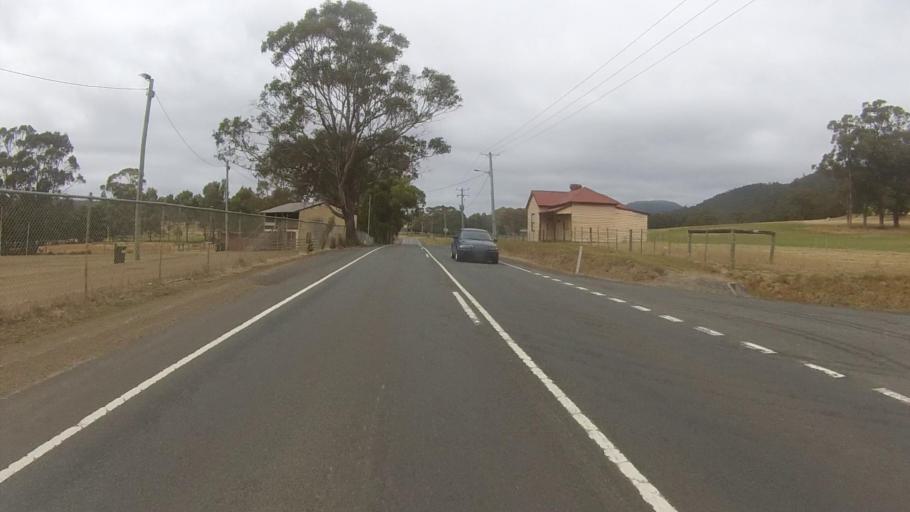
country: AU
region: Tasmania
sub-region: Kingborough
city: Margate
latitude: -42.9885
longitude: 147.1974
